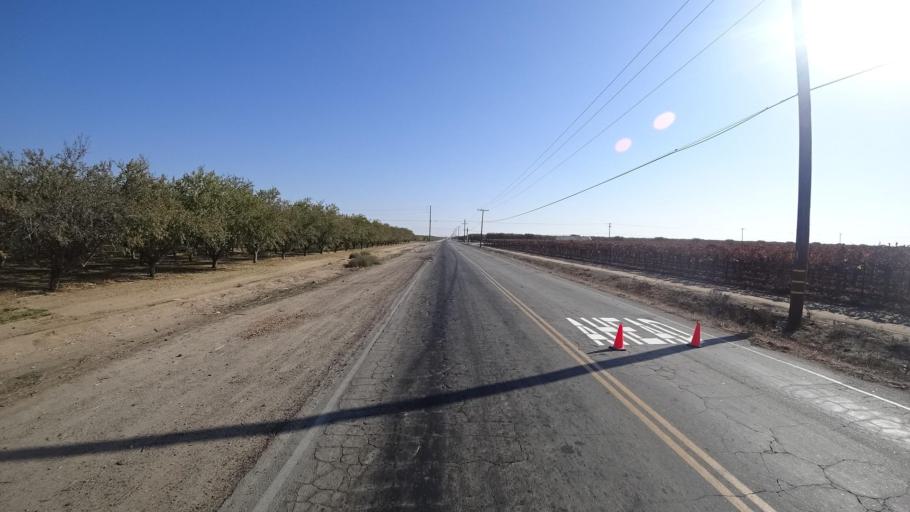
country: US
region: California
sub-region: Kern County
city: McFarland
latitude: 35.7180
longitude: -119.2251
